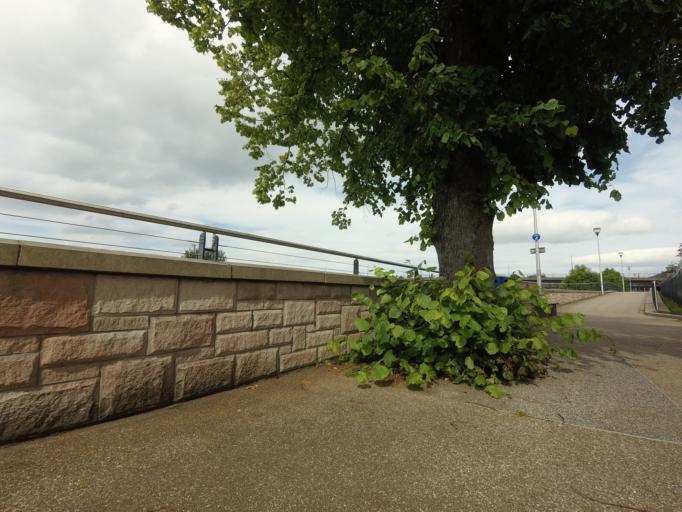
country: GB
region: Scotland
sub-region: Highland
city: Inverness
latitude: 57.4809
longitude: -4.2322
